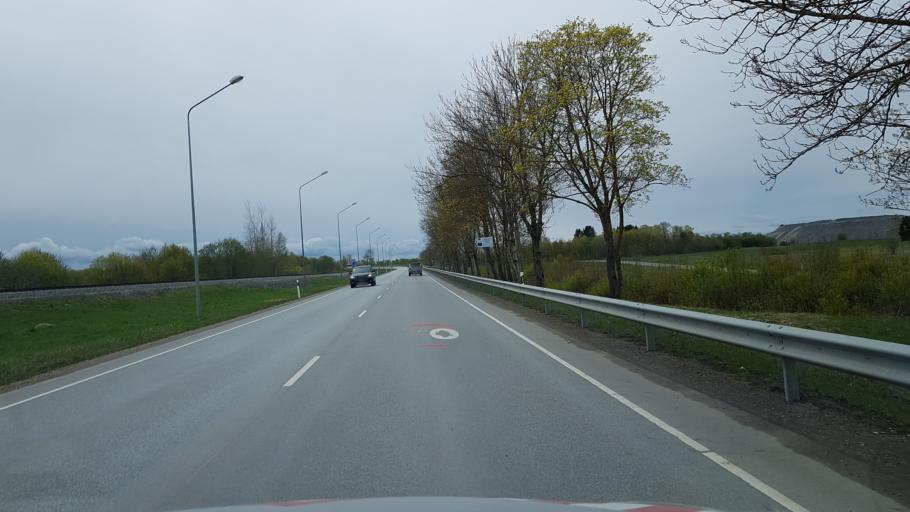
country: EE
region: Ida-Virumaa
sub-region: Johvi vald
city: Johvi
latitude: 59.3469
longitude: 27.4064
